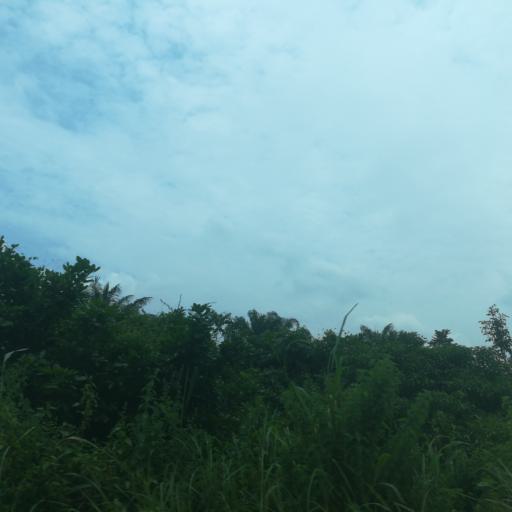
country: NG
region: Lagos
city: Ejirin
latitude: 6.6503
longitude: 3.8284
